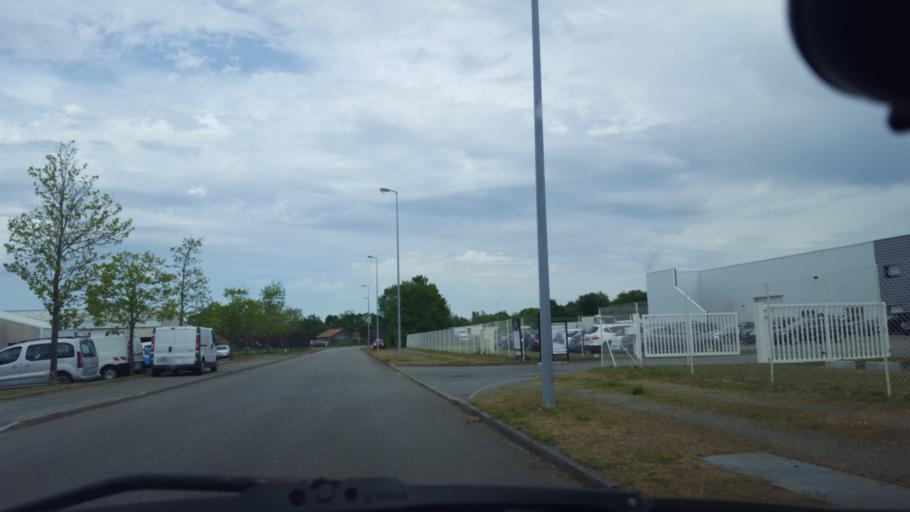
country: FR
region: Pays de la Loire
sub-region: Departement de la Loire-Atlantique
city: Machecoul
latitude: 46.9830
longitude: -1.8073
